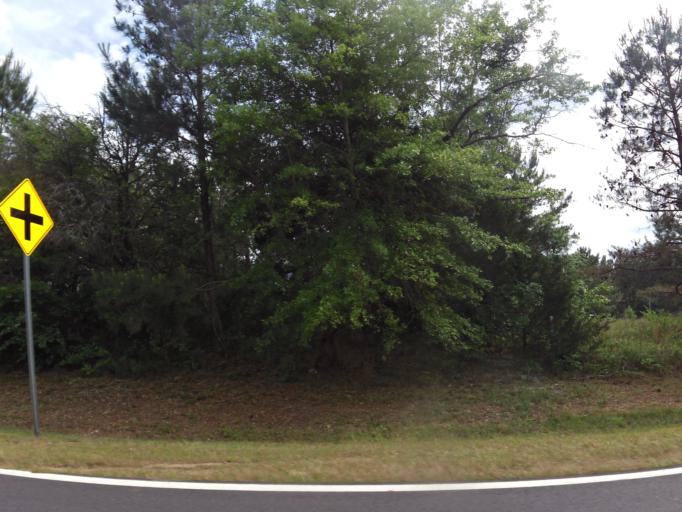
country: US
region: Georgia
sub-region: McDuffie County
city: Thomson
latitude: 33.5232
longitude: -82.4360
